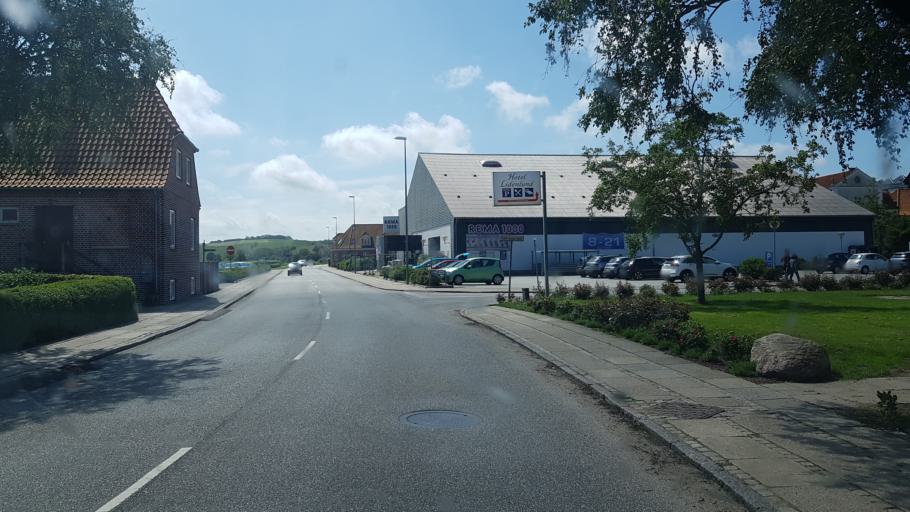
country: DK
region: Central Jutland
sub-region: Lemvig Kommune
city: Lemvig
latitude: 56.5494
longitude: 8.3124
